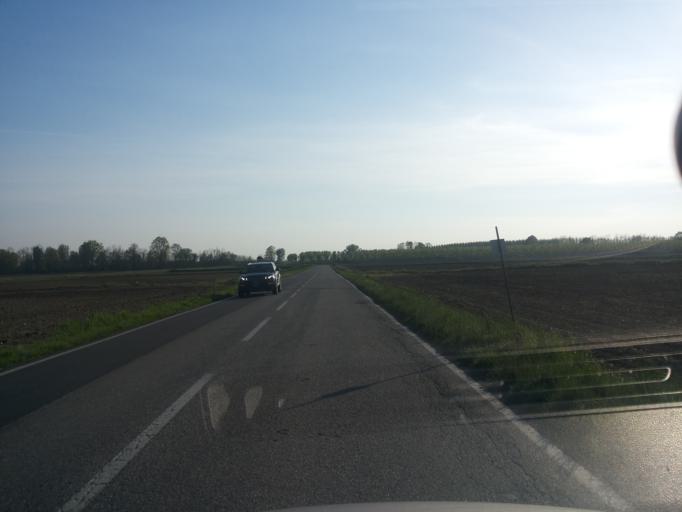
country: IT
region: Lombardy
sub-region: Provincia di Pavia
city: Zeme
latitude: 45.2071
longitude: 8.6418
